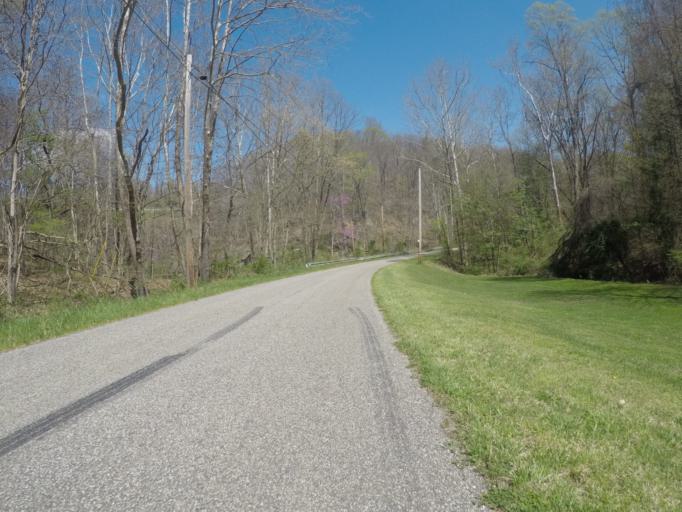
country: US
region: Ohio
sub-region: Lawrence County
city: Burlington
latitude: 38.3929
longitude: -82.5296
